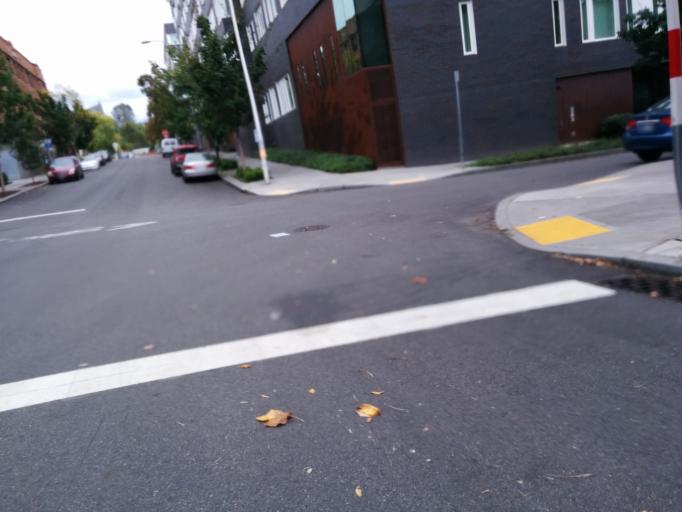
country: US
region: Washington
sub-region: King County
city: Seattle
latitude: 47.6569
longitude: -122.3157
